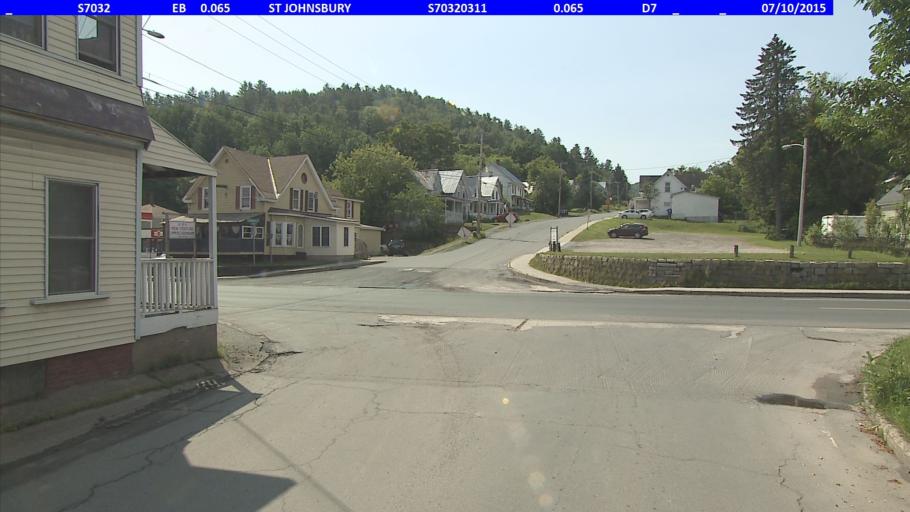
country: US
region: Vermont
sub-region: Caledonia County
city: Saint Johnsbury
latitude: 44.4206
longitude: -72.0109
